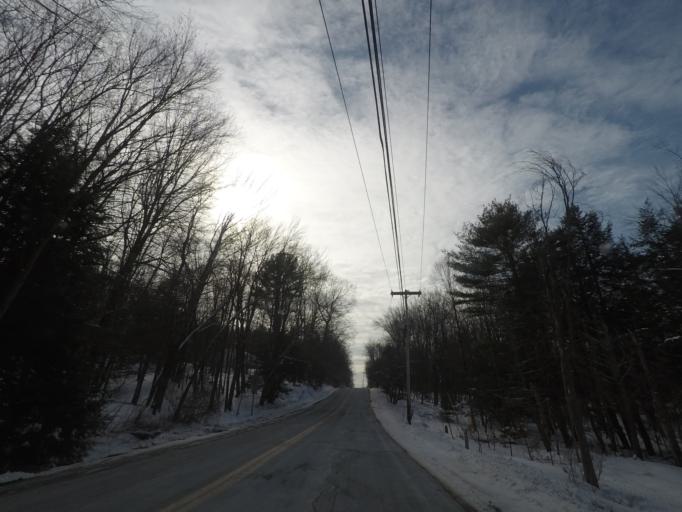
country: US
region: New York
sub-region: Rensselaer County
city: Averill Park
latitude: 42.5699
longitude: -73.4912
